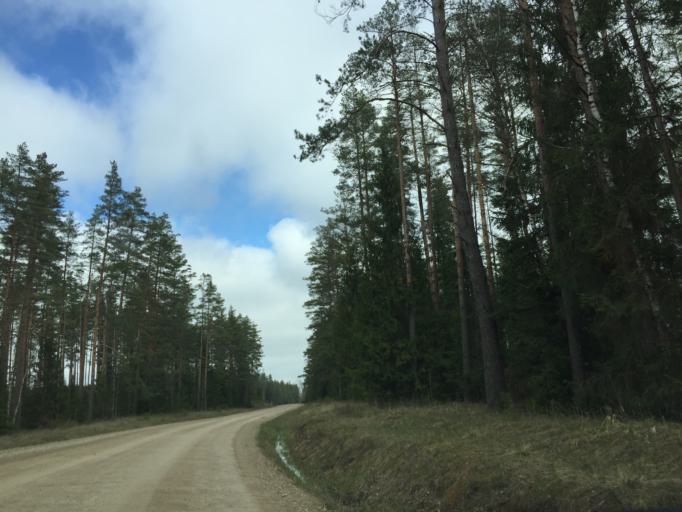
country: EE
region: Valgamaa
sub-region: Valga linn
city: Valga
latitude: 57.6154
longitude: 26.2357
